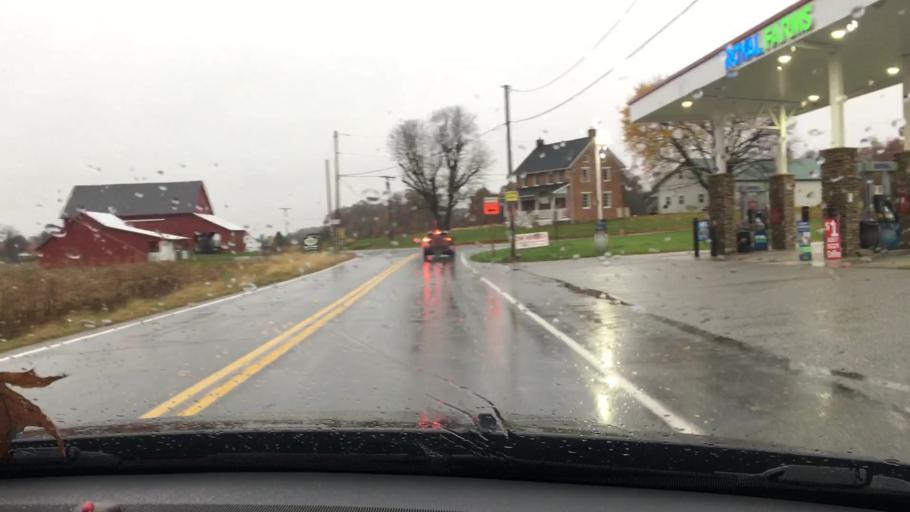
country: US
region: Pennsylvania
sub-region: York County
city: Stewartstown
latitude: 39.7218
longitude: -76.5438
